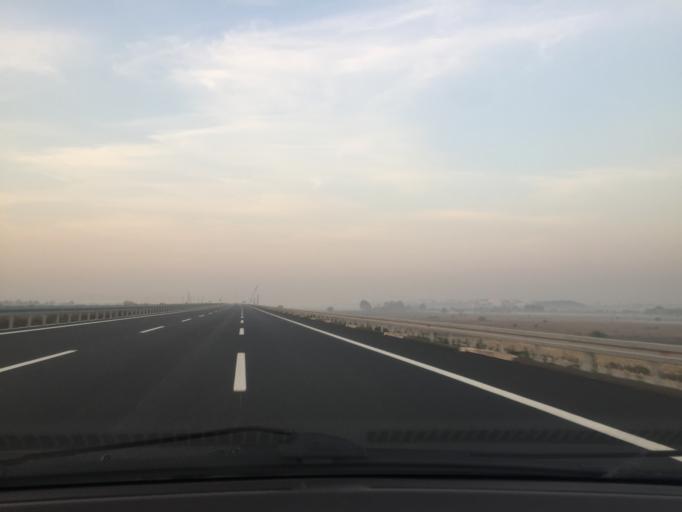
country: TR
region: Bursa
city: Karacabey
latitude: 40.2274
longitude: 28.4094
